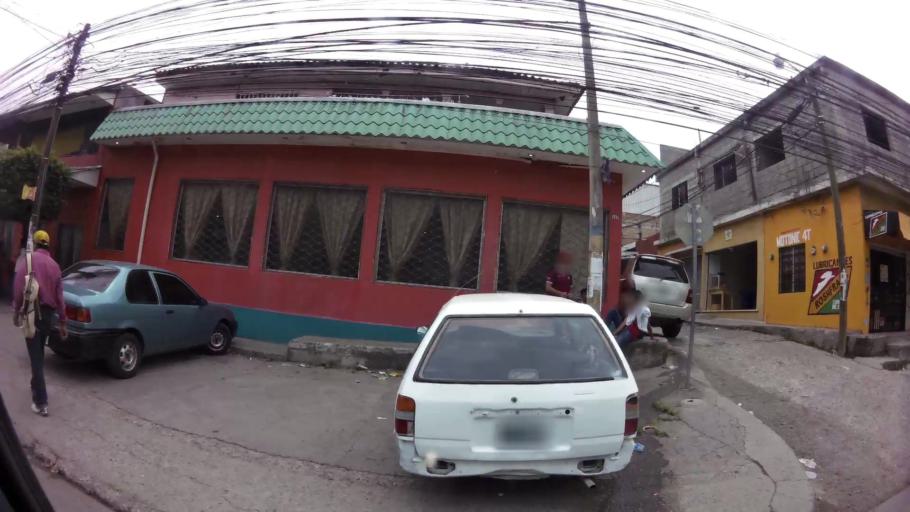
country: HN
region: Francisco Morazan
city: Tegucigalpa
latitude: 14.0639
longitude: -87.2070
